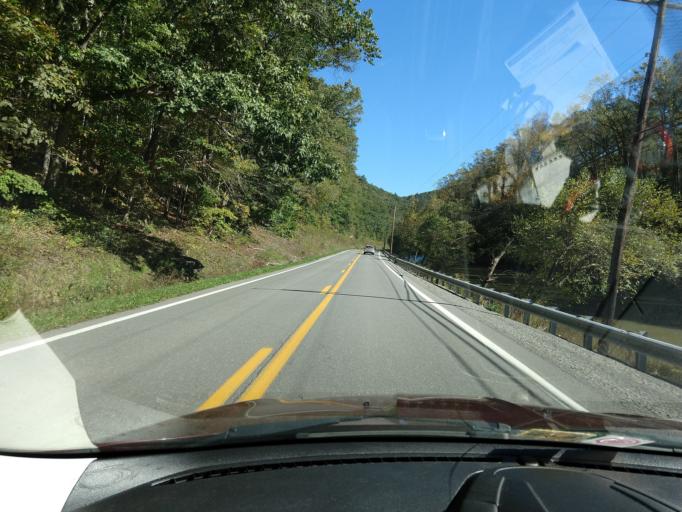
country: US
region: West Virginia
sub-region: Pocahontas County
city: Marlinton
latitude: 38.2130
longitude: -80.0609
